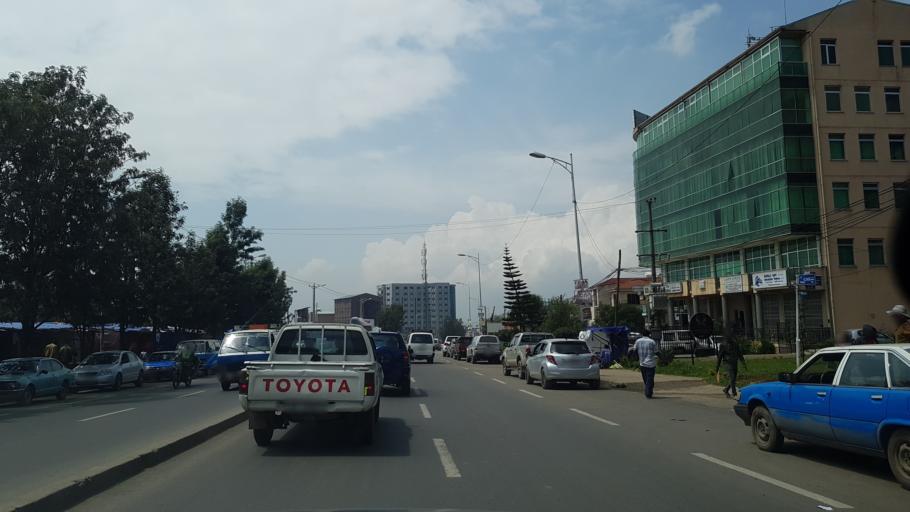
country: ET
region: Adis Abeba
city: Addis Ababa
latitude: 9.0243
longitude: 38.8265
